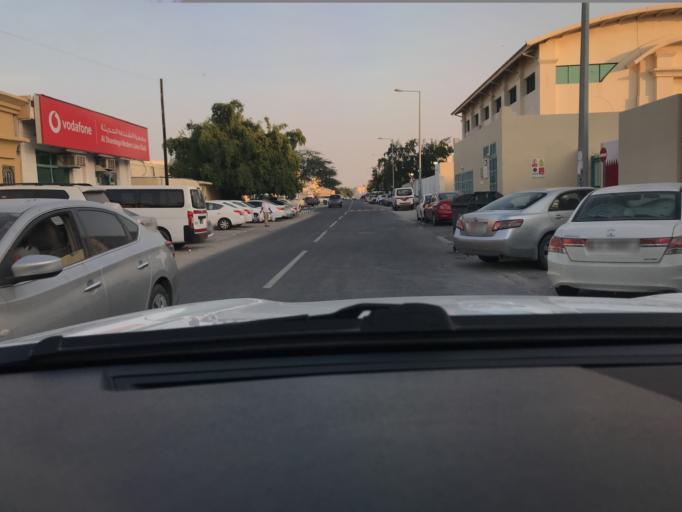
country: QA
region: Baladiyat ad Dawhah
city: Doha
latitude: 25.2534
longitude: 51.5024
